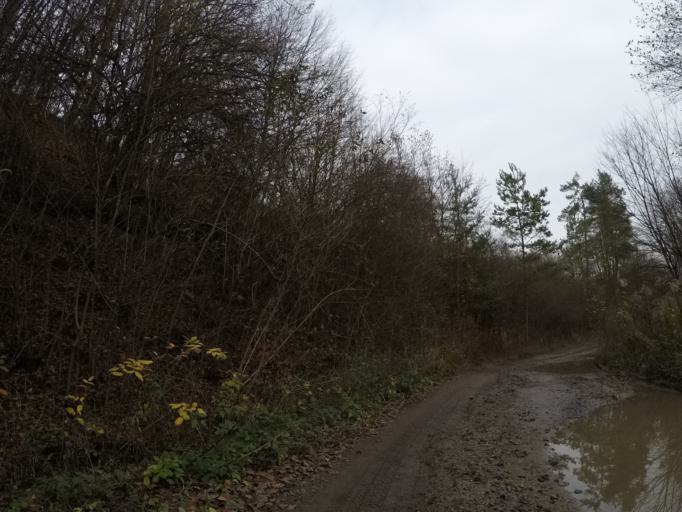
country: SK
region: Presovsky
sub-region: Okres Presov
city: Presov
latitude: 48.8984
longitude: 21.1872
